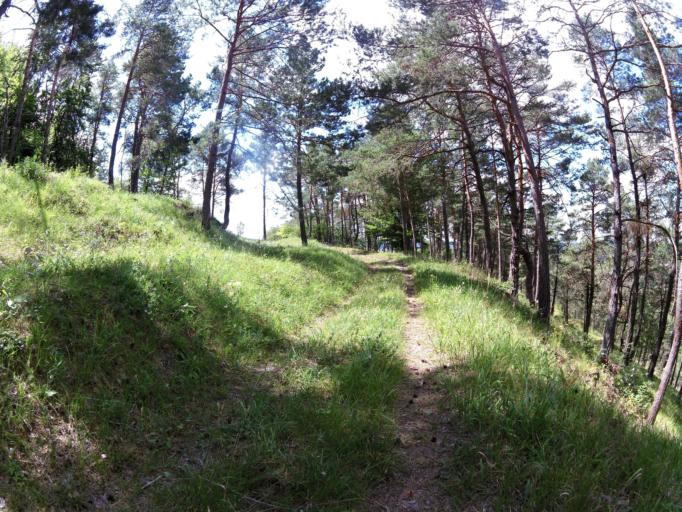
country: DE
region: Bavaria
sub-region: Regierungsbezirk Unterfranken
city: Thungersheim
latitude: 49.8920
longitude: 9.8442
